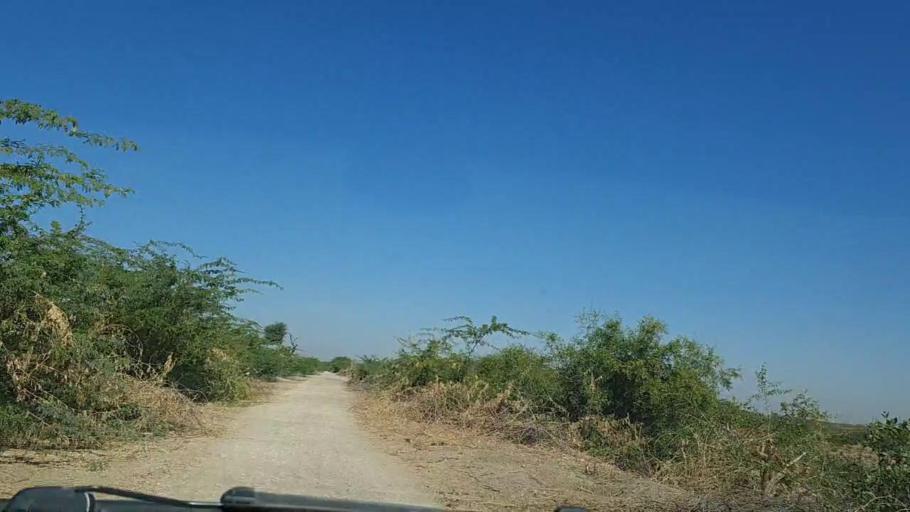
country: PK
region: Sindh
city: Dhoro Naro
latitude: 25.4636
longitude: 69.5134
